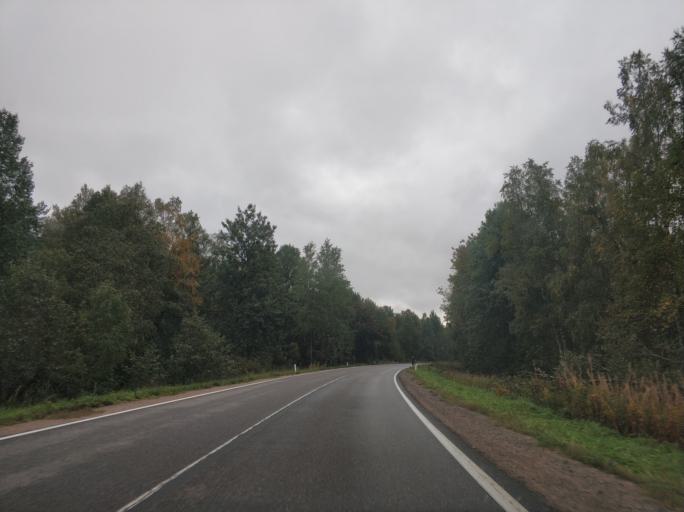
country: RU
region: Leningrad
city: Borisova Griva
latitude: 60.1329
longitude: 30.9624
